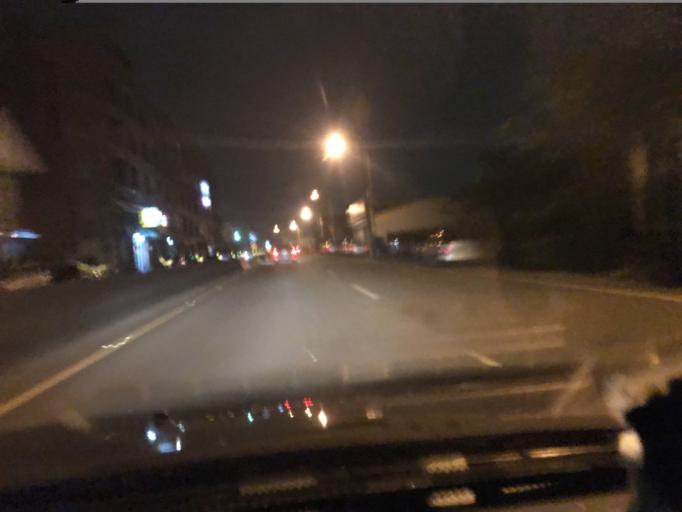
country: TW
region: Taiwan
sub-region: Hsinchu
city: Zhubei
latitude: 24.7959
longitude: 121.0561
